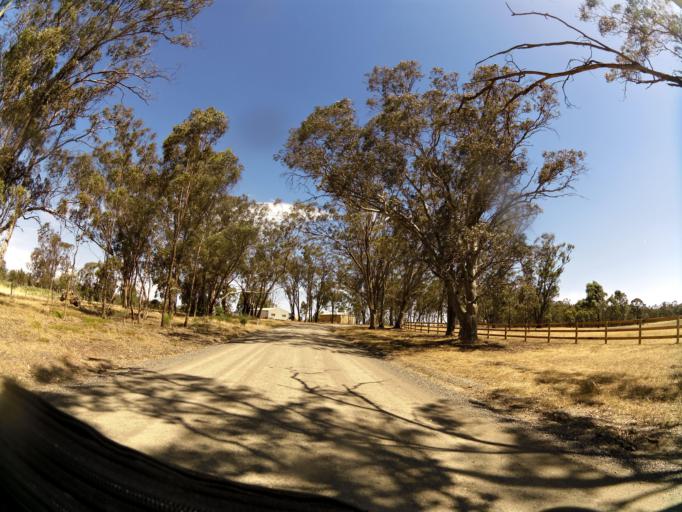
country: AU
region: Victoria
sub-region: Campaspe
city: Kyabram
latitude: -36.8384
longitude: 145.0743
